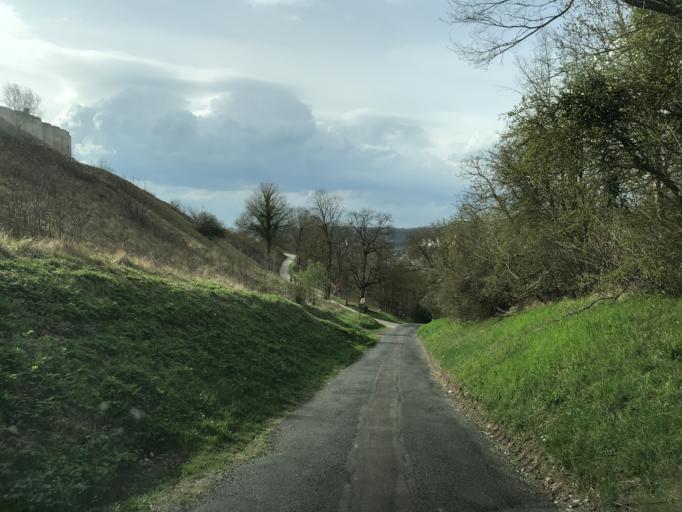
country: FR
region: Haute-Normandie
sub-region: Departement de l'Eure
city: Les Andelys
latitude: 49.2381
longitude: 1.4051
